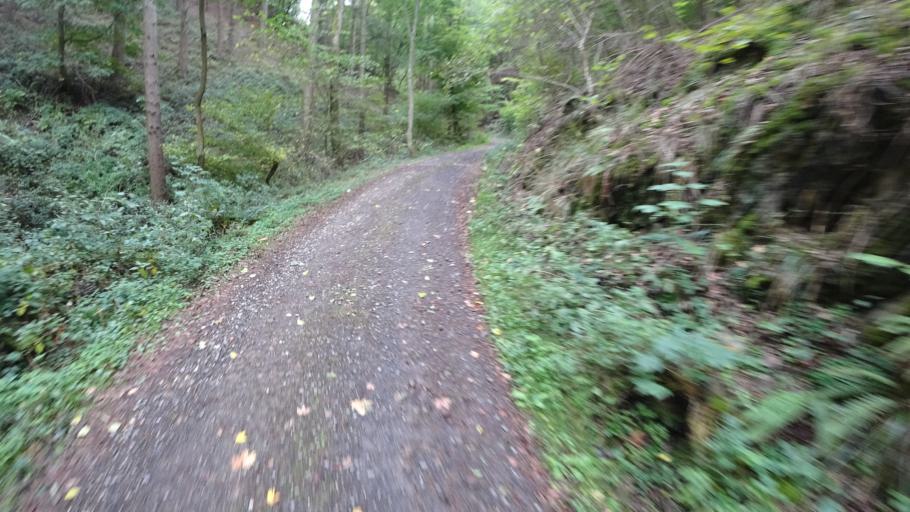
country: DE
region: Rheinland-Pfalz
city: Kratzenburg
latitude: 50.2216
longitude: 7.5422
